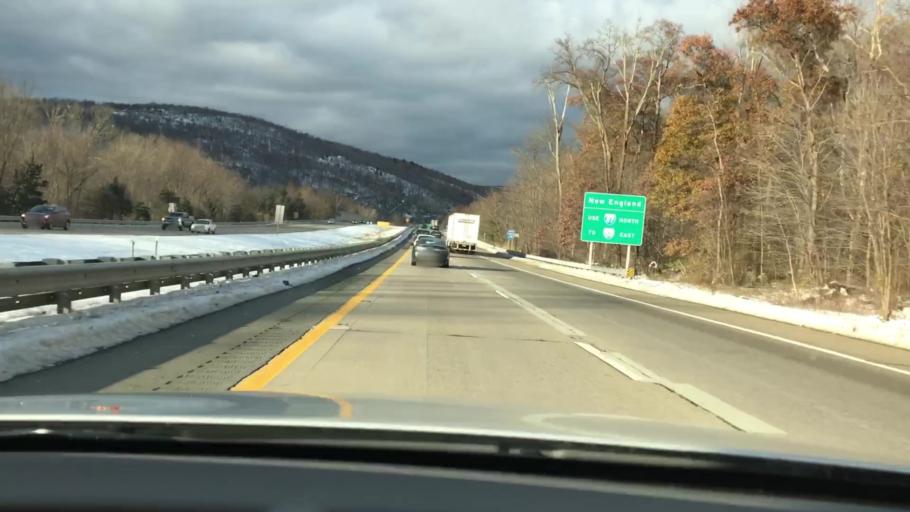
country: US
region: New Jersey
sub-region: Bergen County
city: Mahwah
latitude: 41.0896
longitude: -74.1682
